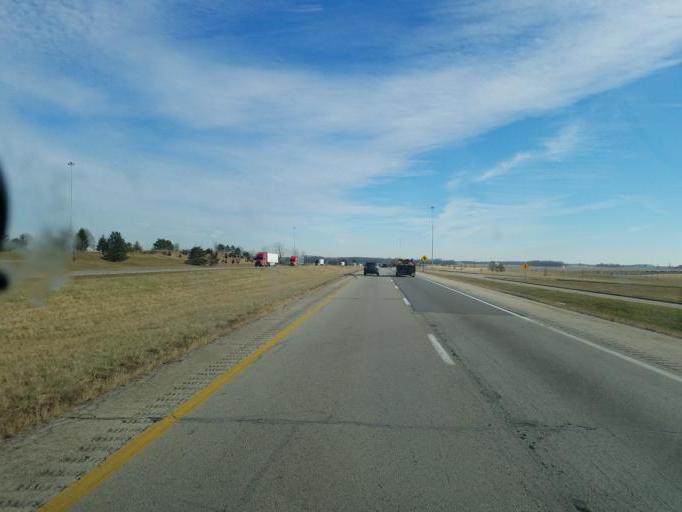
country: US
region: Ohio
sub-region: Preble County
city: New Paris
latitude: 39.8285
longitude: -84.7597
